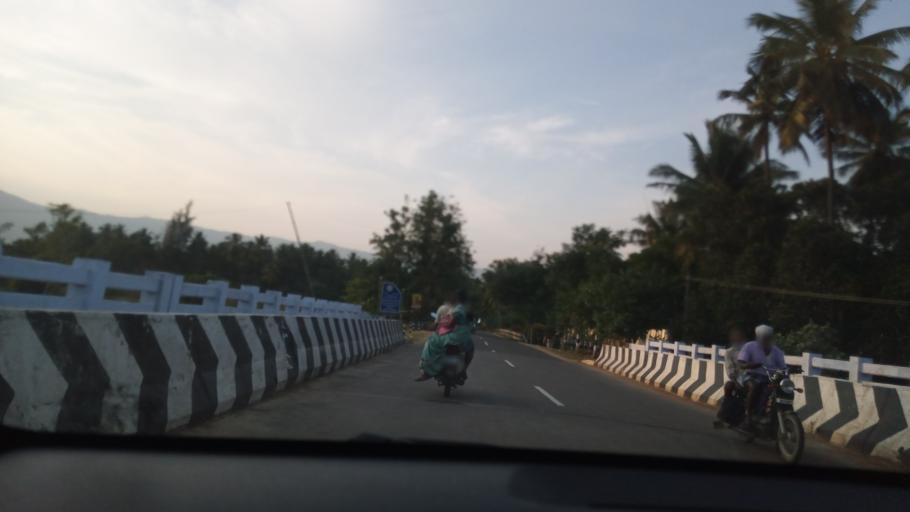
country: IN
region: Tamil Nadu
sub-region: Coimbatore
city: Perur
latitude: 10.9485
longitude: 76.7694
